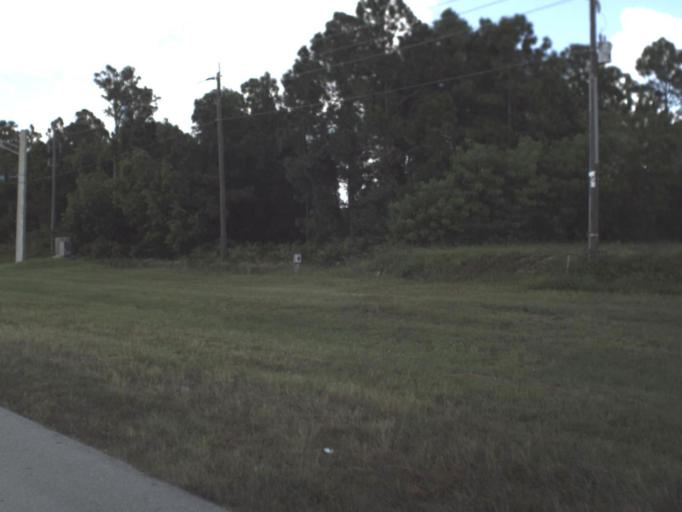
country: US
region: Florida
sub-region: Lee County
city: Gateway
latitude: 26.6077
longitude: -81.7552
